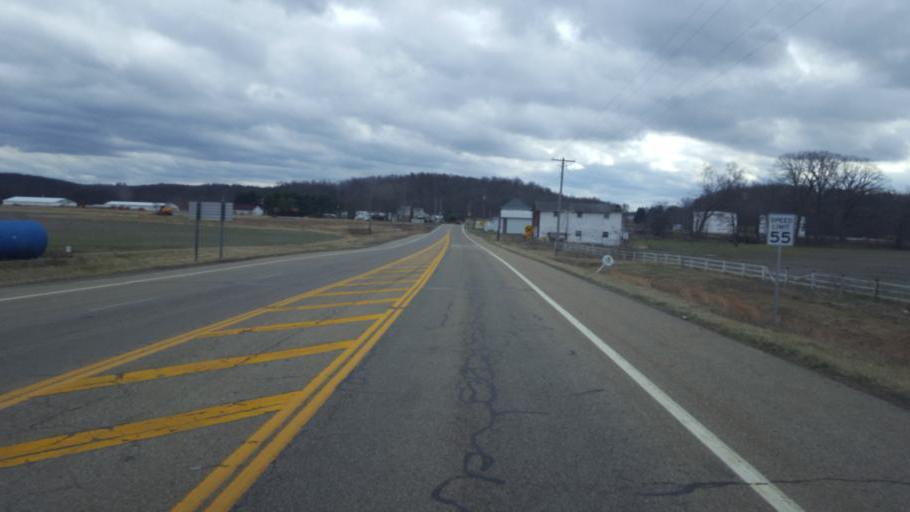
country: US
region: Ohio
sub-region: Muskingum County
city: Frazeysburg
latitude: 40.1018
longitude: -82.1734
